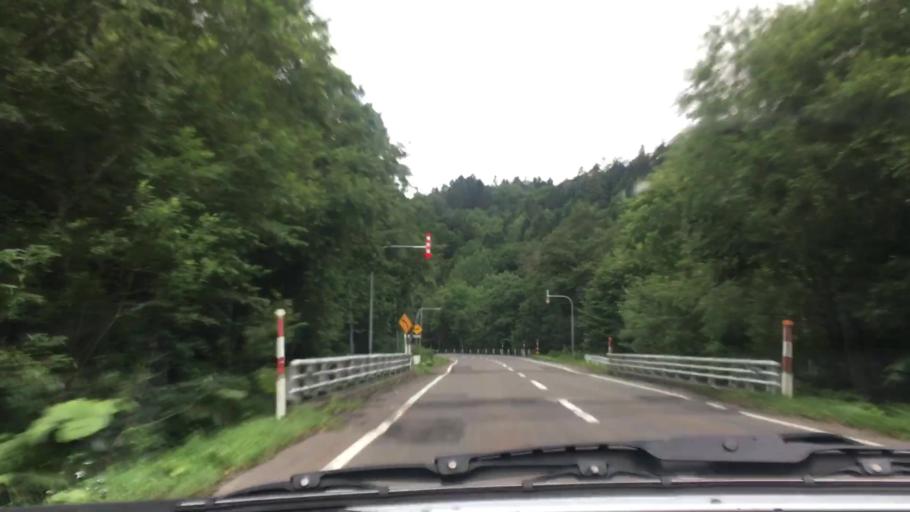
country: JP
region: Hokkaido
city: Shimo-furano
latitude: 43.0702
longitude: 142.6696
